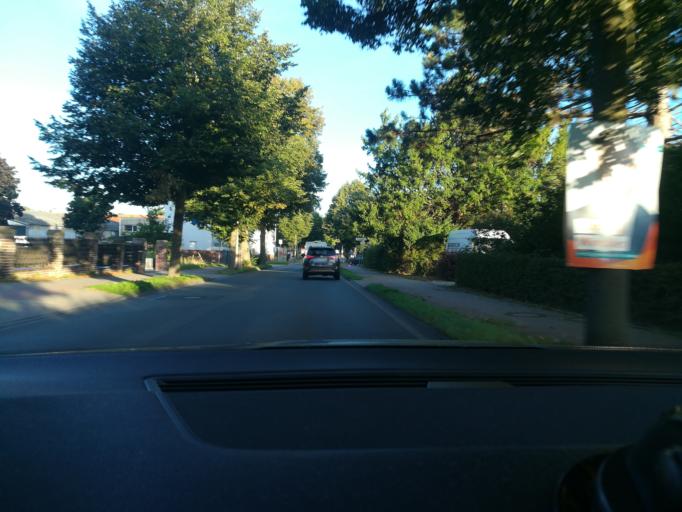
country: DE
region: North Rhine-Westphalia
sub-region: Regierungsbezirk Detmold
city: Minden
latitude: 52.3353
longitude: 8.8787
